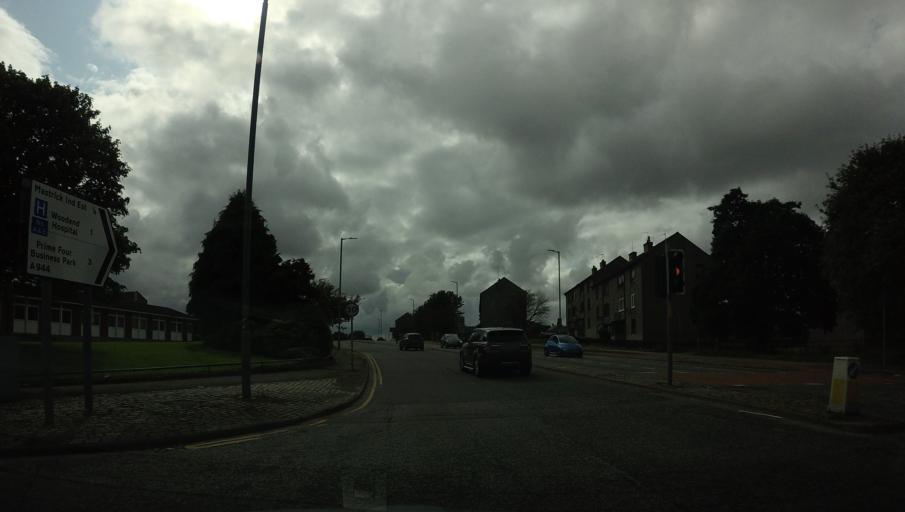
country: GB
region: Scotland
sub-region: Aberdeen City
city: Cults
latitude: 57.1523
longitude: -2.1498
